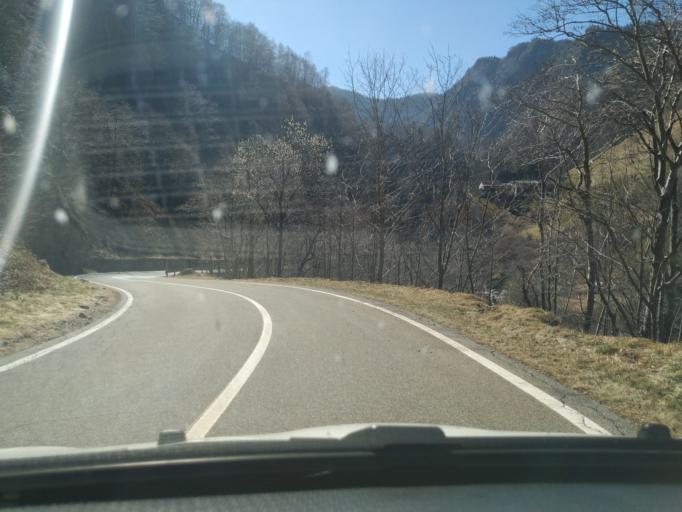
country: IT
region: Piedmont
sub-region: Provincia di Vercelli
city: Cervatto
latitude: 45.8870
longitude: 8.1784
